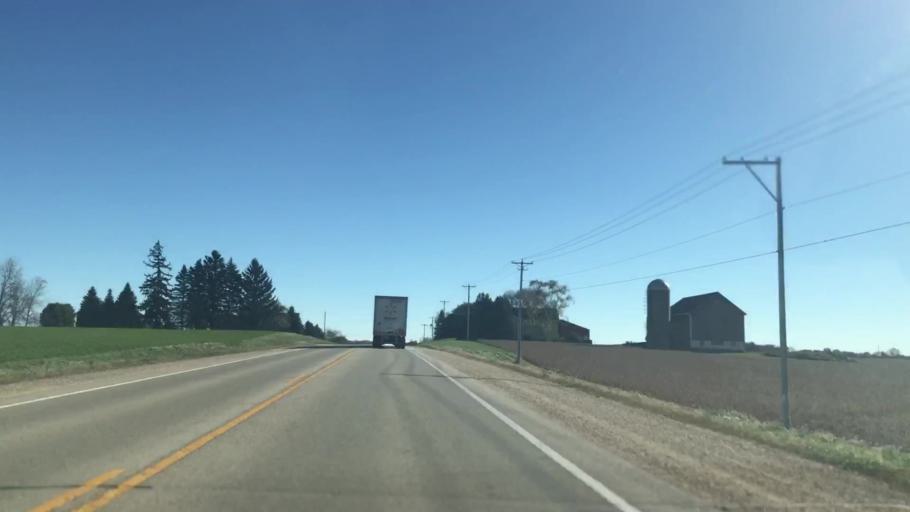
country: US
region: Wisconsin
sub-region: Dodge County
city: Juneau
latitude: 43.4447
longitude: -88.7254
